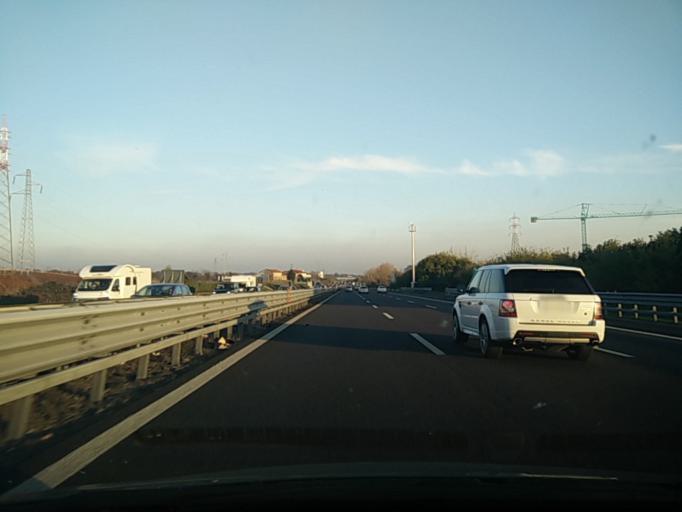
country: IT
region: Veneto
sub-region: Provincia di Verona
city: Cavalcaselle
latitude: 45.4287
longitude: 10.7367
